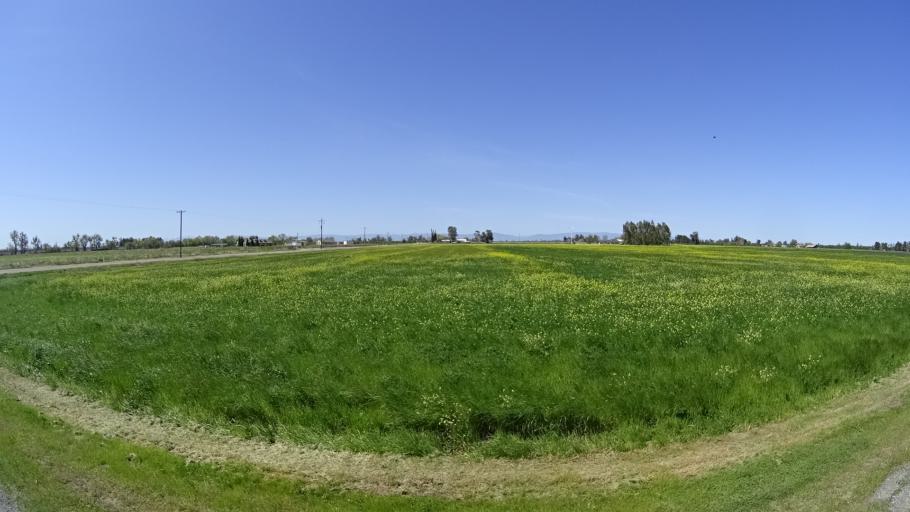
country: US
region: California
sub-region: Glenn County
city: Hamilton City
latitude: 39.7901
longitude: -122.0570
